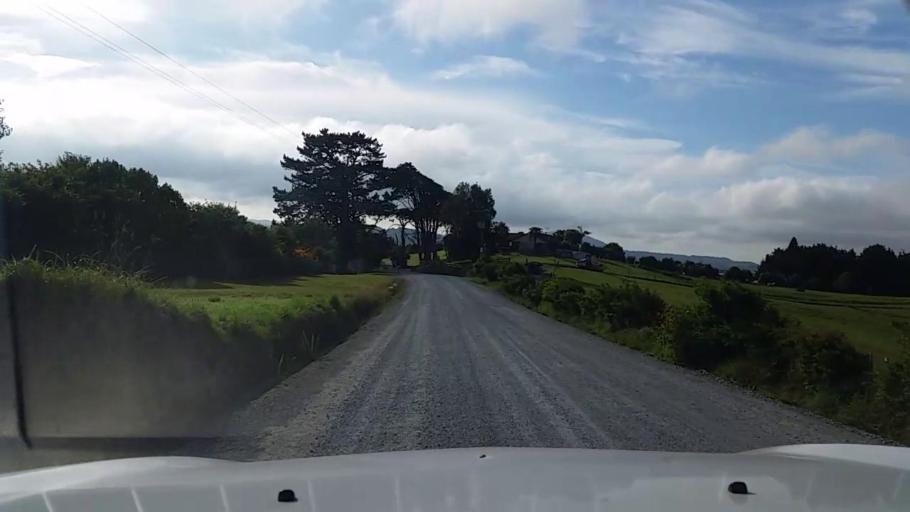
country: NZ
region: Northland
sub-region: Whangarei
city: Maungatapere
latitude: -35.6822
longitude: 174.1790
